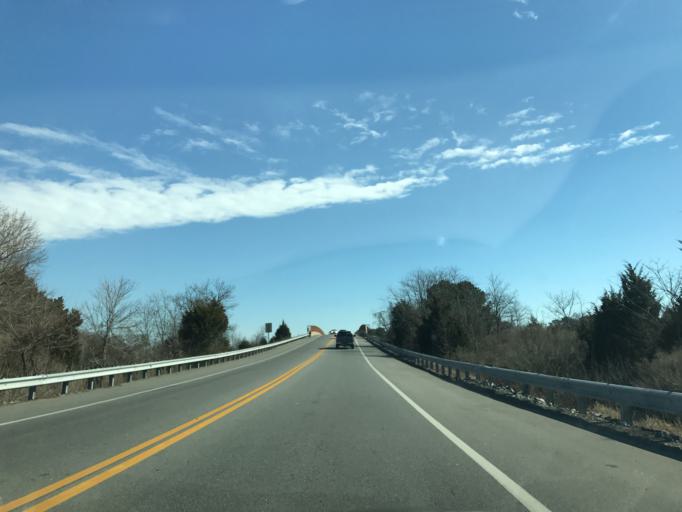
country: US
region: Maryland
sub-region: Queen Anne's County
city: Chester
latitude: 38.9771
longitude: -76.2858
